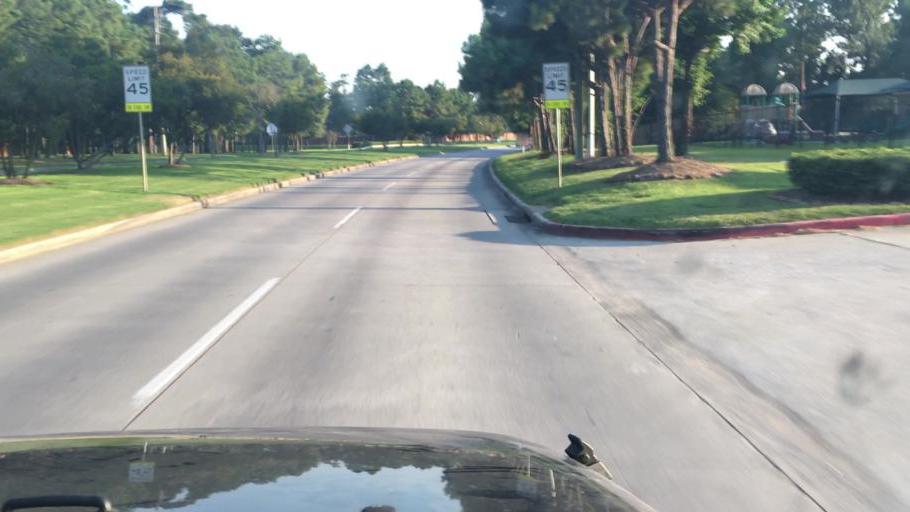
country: US
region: Texas
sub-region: Harris County
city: Atascocita
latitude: 29.9611
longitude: -95.1683
